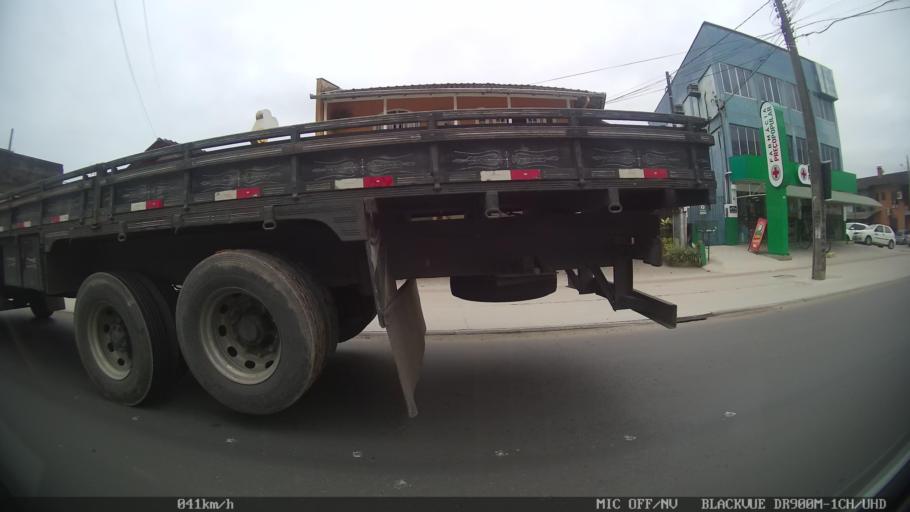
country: BR
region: Santa Catarina
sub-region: Joinville
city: Joinville
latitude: -26.3018
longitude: -48.8227
